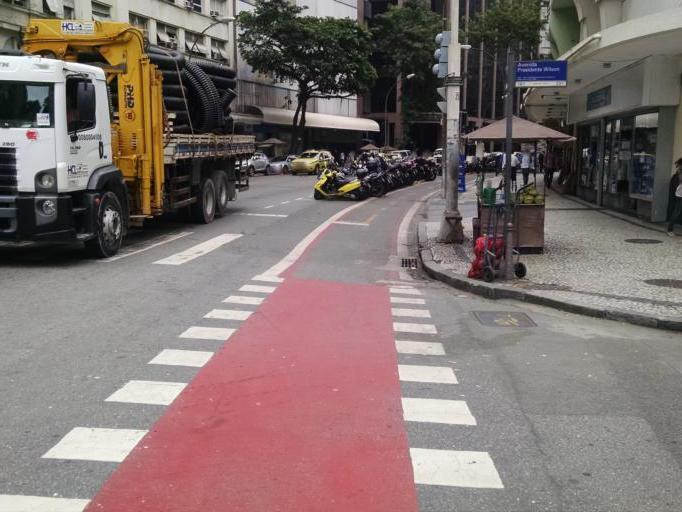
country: BR
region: Rio de Janeiro
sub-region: Rio De Janeiro
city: Rio de Janeiro
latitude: -22.9112
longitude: -43.1733
